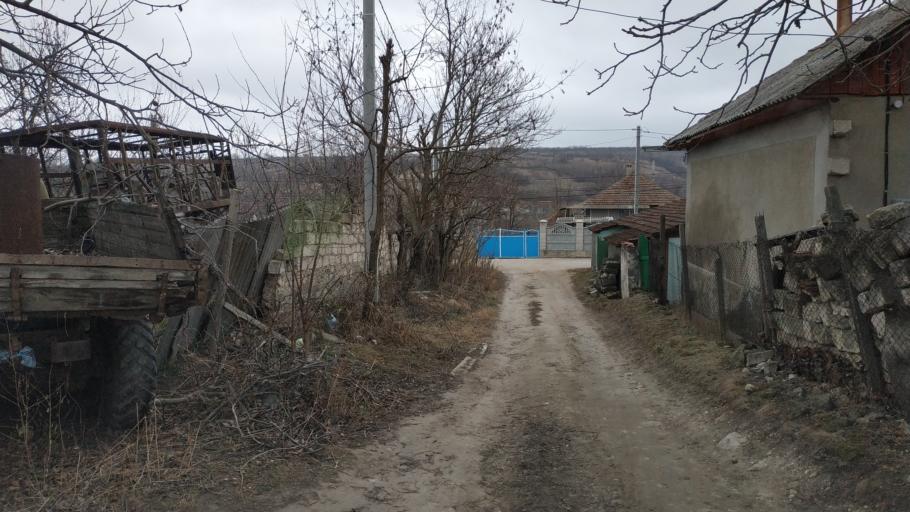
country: MD
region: Laloveni
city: Ialoveni
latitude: 46.9019
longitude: 28.8035
